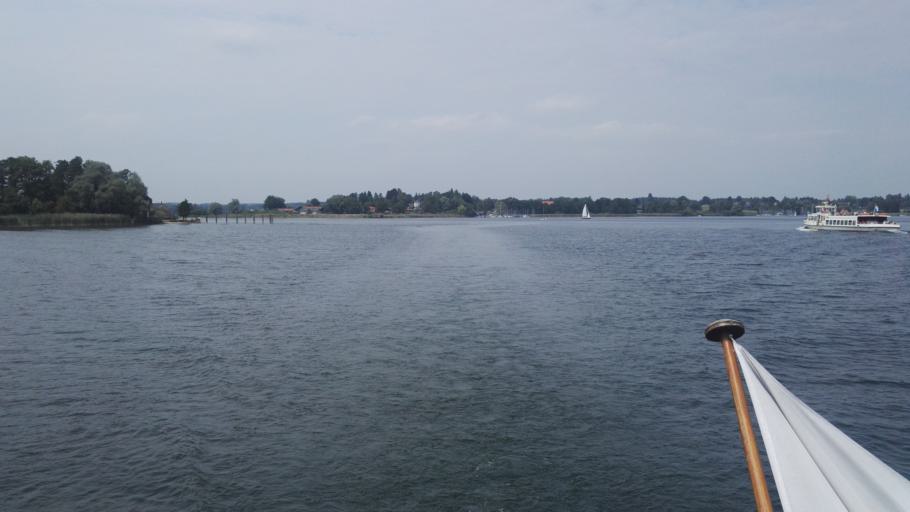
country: DE
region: Bavaria
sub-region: Upper Bavaria
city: Chiemsee
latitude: 47.8709
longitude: 12.3973
